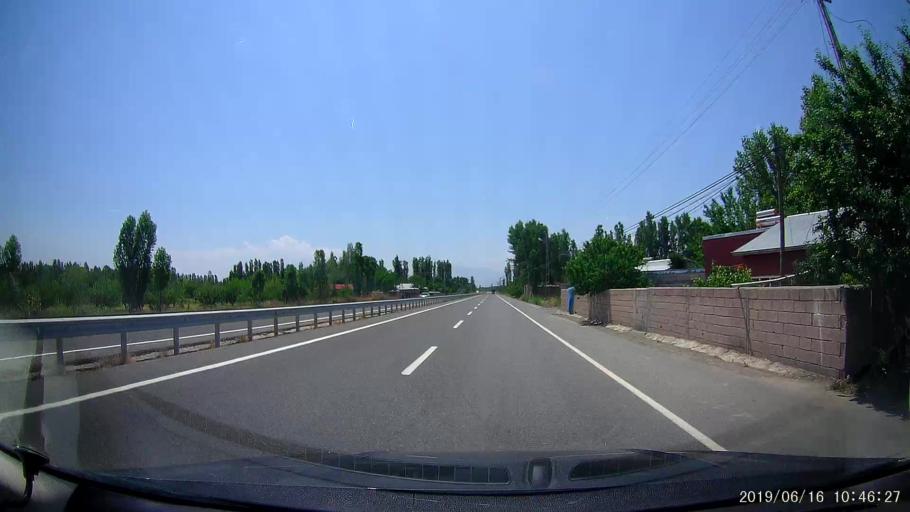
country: AM
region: Armavir
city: Shenavan
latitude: 40.0216
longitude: 43.8793
